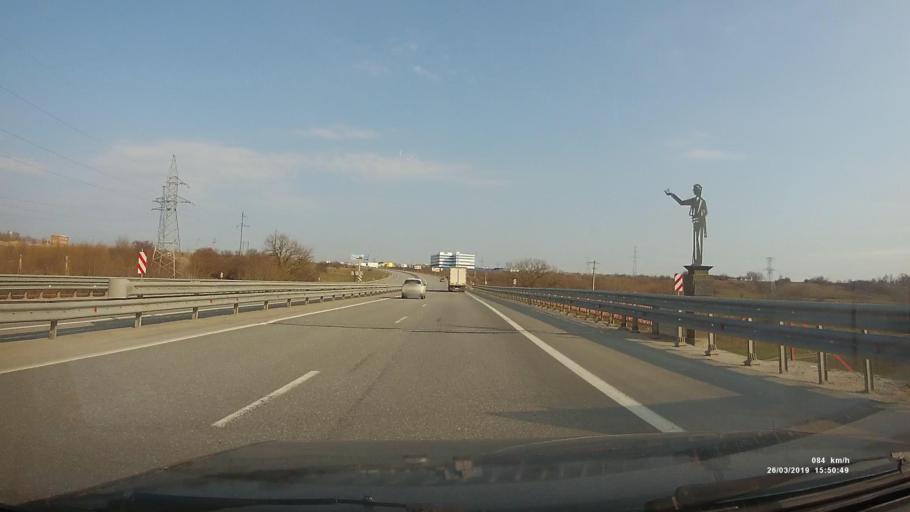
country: RU
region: Rostov
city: Chaltyr
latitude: 47.2714
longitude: 39.4938
